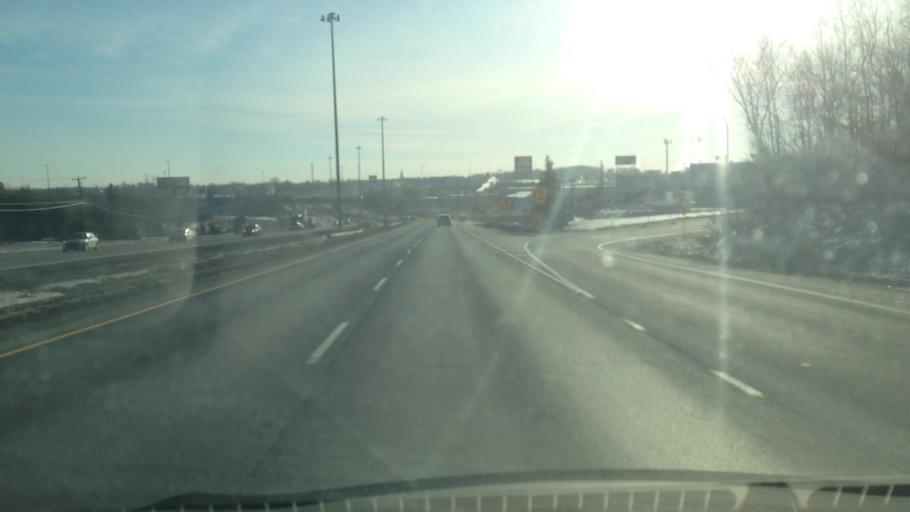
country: CA
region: Quebec
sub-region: Laurentides
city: Saint-Jerome
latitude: 45.7994
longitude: -74.0301
